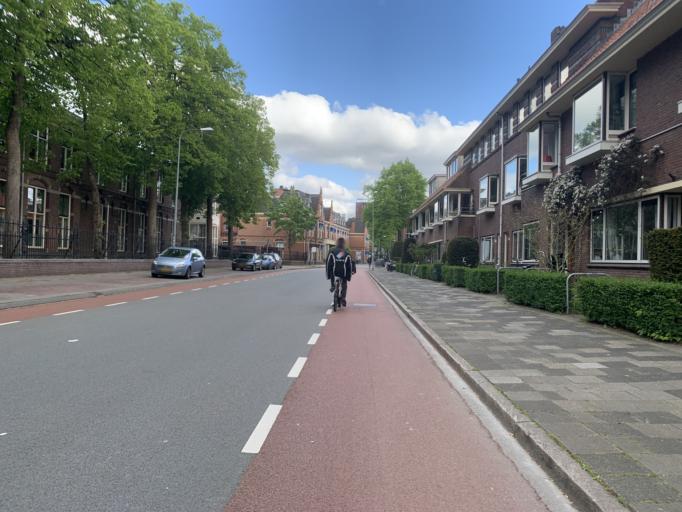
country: NL
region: Groningen
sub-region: Gemeente Groningen
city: Groningen
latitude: 53.2219
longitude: 6.5731
